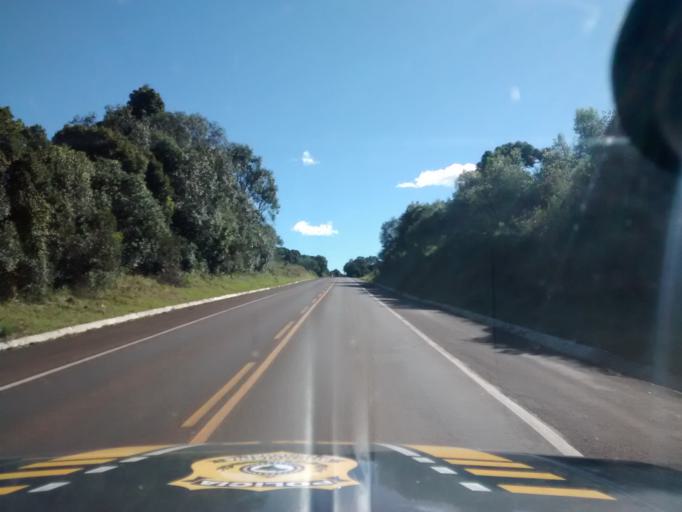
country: BR
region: Rio Grande do Sul
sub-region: Vacaria
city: Vacaria
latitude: -28.3324
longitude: -51.1718
